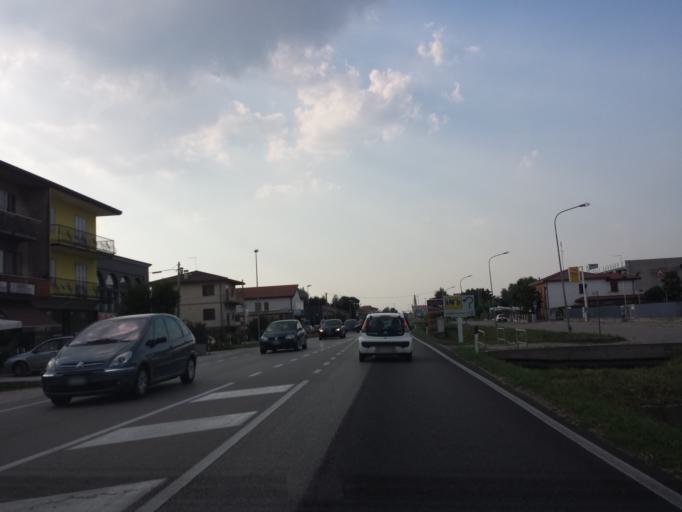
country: IT
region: Veneto
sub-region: Provincia di Padova
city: Mestrino
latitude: 45.4347
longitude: 11.7715
